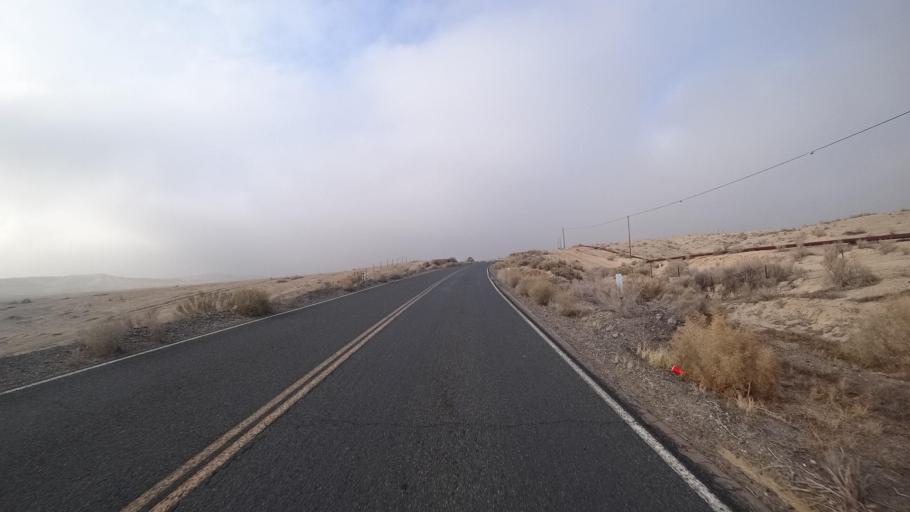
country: US
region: California
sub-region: Kern County
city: Ford City
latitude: 35.2468
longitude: -119.4603
